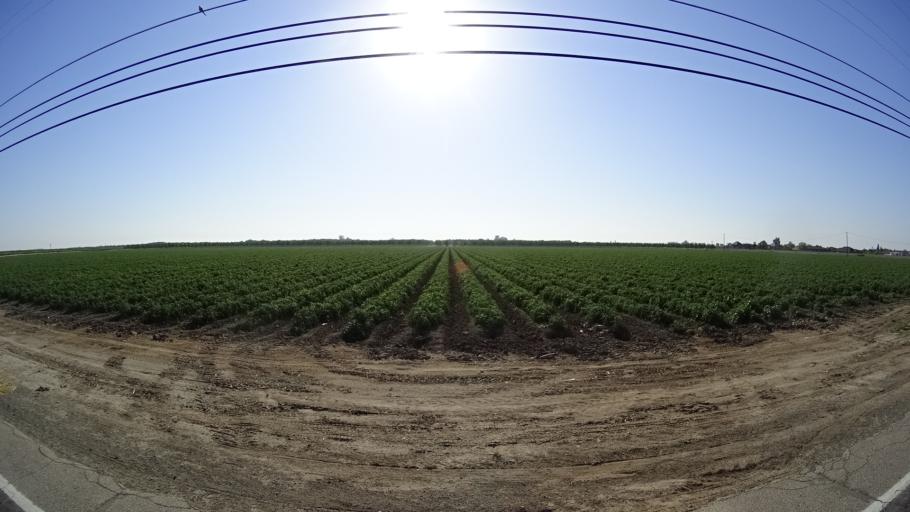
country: US
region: California
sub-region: Kings County
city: Armona
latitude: 36.3521
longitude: -119.7090
